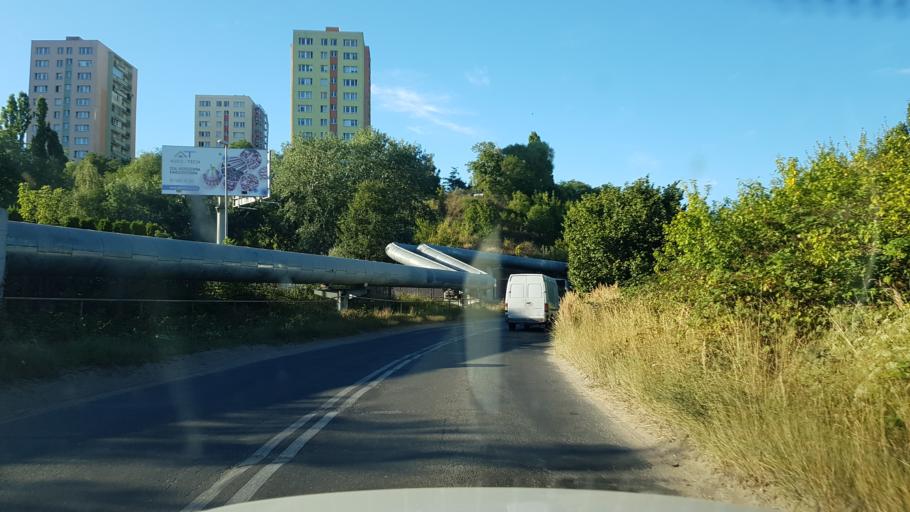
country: PL
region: West Pomeranian Voivodeship
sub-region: Szczecin
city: Szczecin
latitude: 53.3991
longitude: 14.5323
